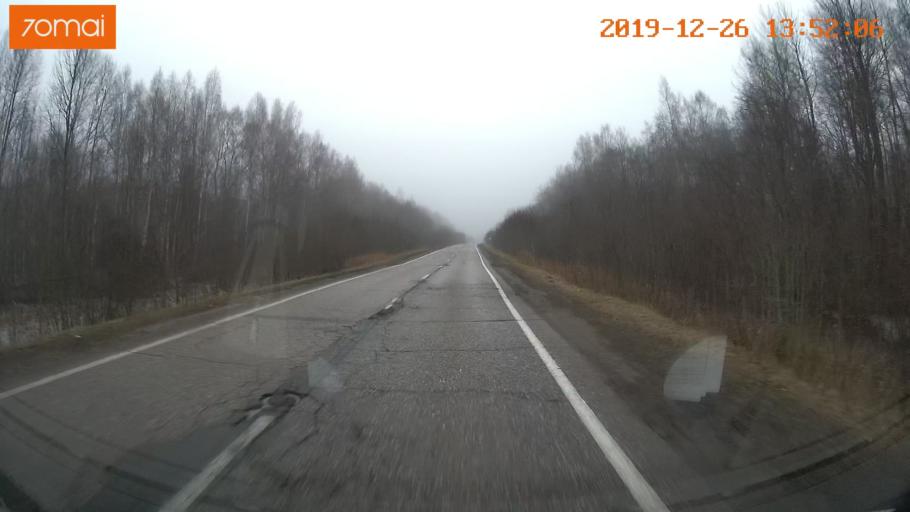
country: RU
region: Jaroslavl
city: Poshekhon'ye
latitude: 58.6362
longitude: 38.5986
